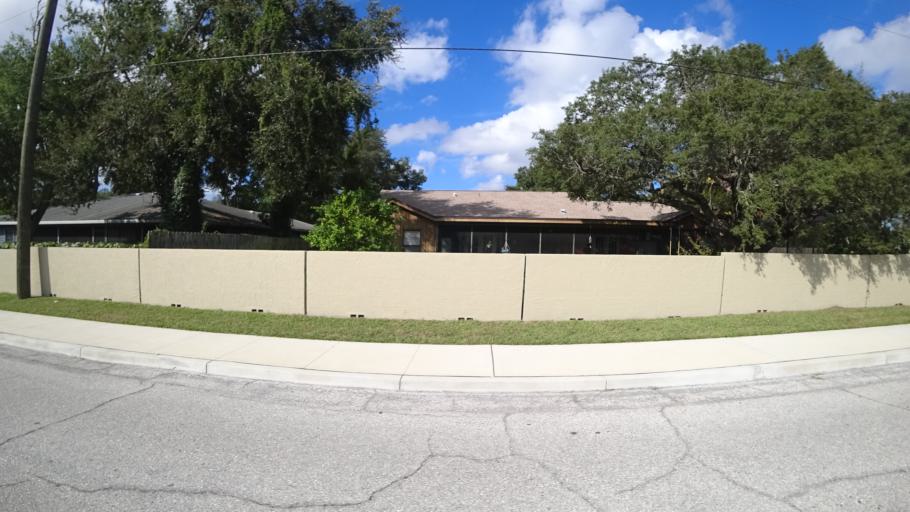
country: US
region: Florida
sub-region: Manatee County
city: West Bradenton
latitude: 27.5007
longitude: -82.6079
